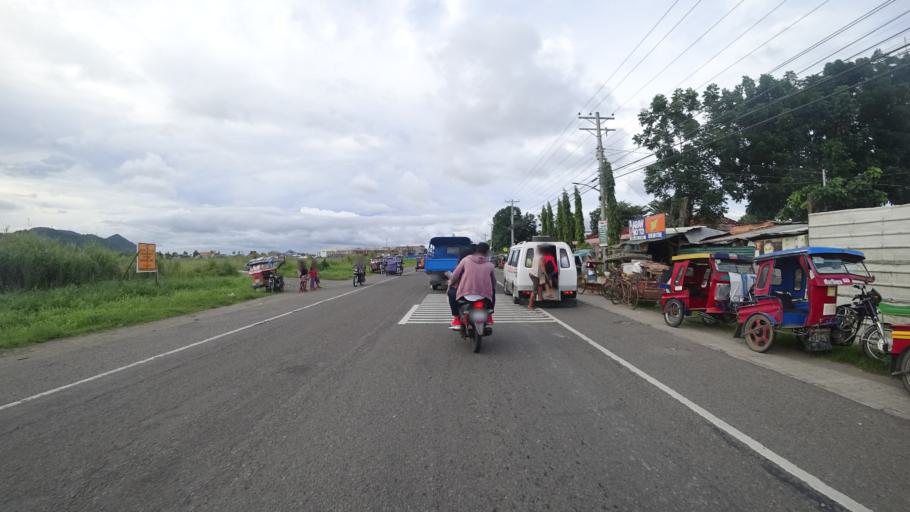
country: PH
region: Eastern Visayas
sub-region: Province of Leyte
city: Pawing
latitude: 11.1749
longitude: 125.0004
